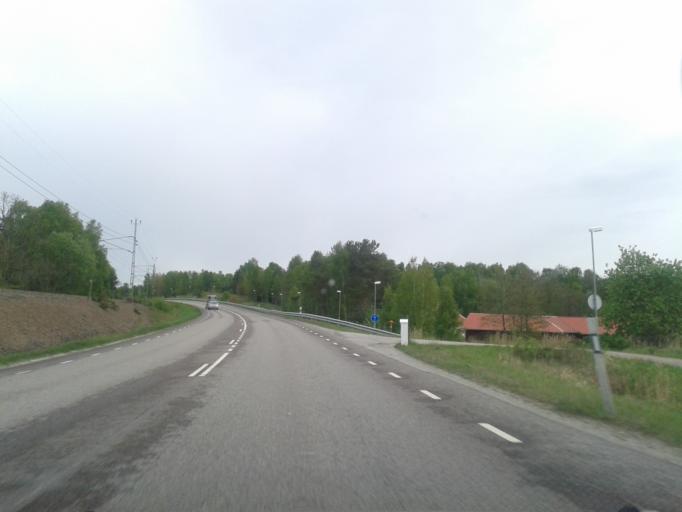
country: SE
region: Vaestra Goetaland
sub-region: Stenungsunds Kommun
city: Stora Hoga
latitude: 58.0012
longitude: 11.8265
